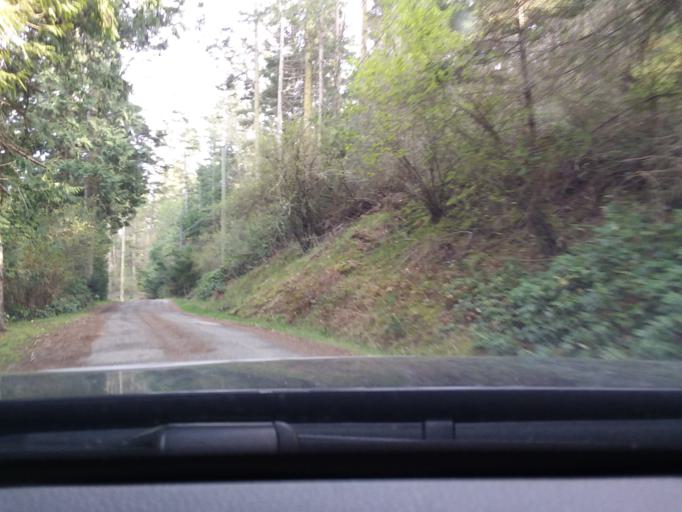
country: CA
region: British Columbia
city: North Saanich
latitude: 48.7410
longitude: -123.2376
